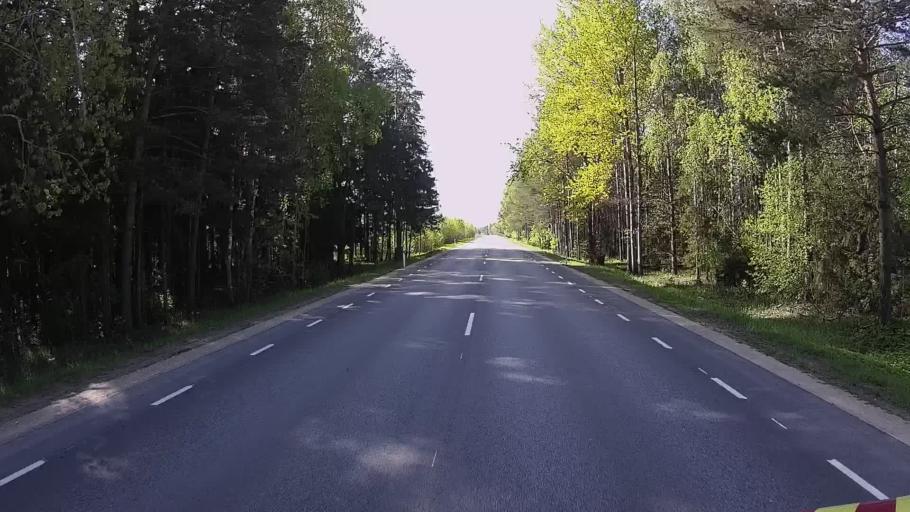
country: EE
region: Tartu
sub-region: UElenurme vald
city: Ulenurme
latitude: 58.3231
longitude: 26.9829
